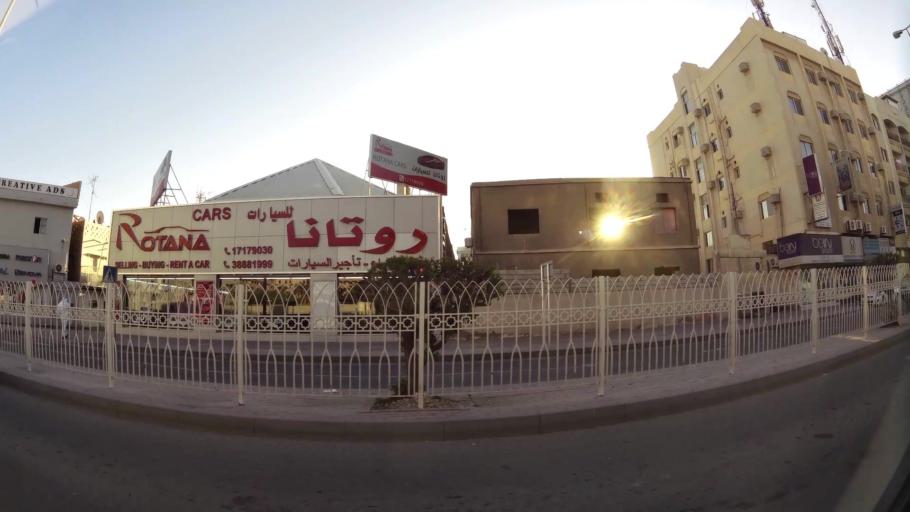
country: BH
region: Manama
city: Manama
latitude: 26.2362
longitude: 50.5874
